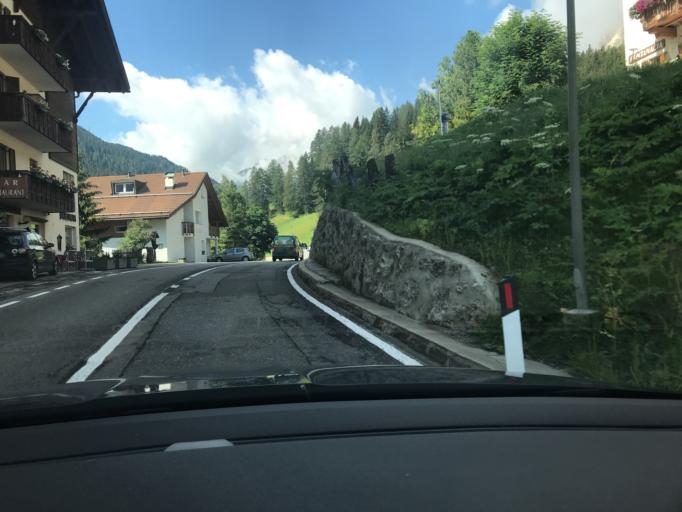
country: IT
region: Trentino-Alto Adige
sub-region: Bolzano
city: Corvara in Badia
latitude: 46.5740
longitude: 11.8926
